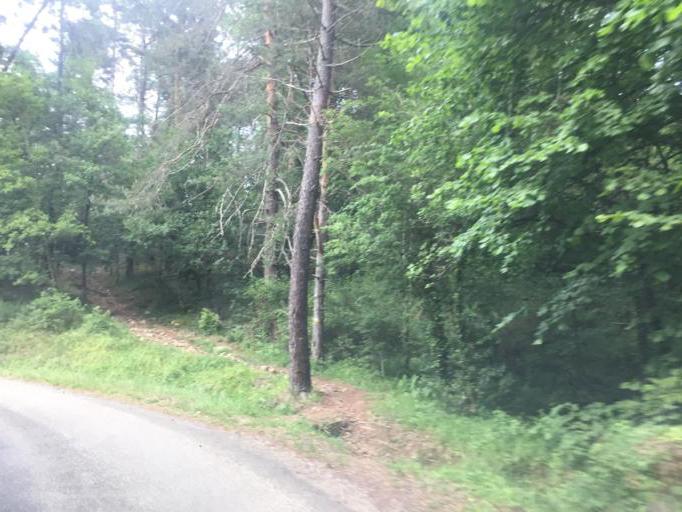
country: FR
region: Rhone-Alpes
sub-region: Departement de l'Ardeche
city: Coux
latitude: 44.7864
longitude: 4.6285
